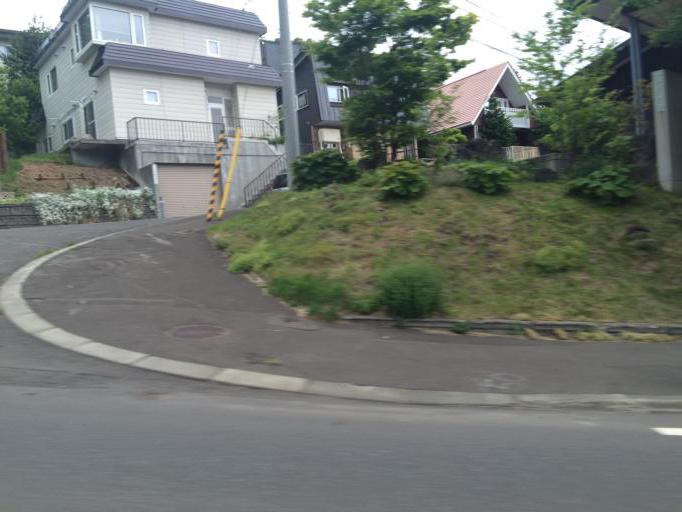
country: JP
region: Hokkaido
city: Sapporo
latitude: 43.0427
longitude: 141.2916
